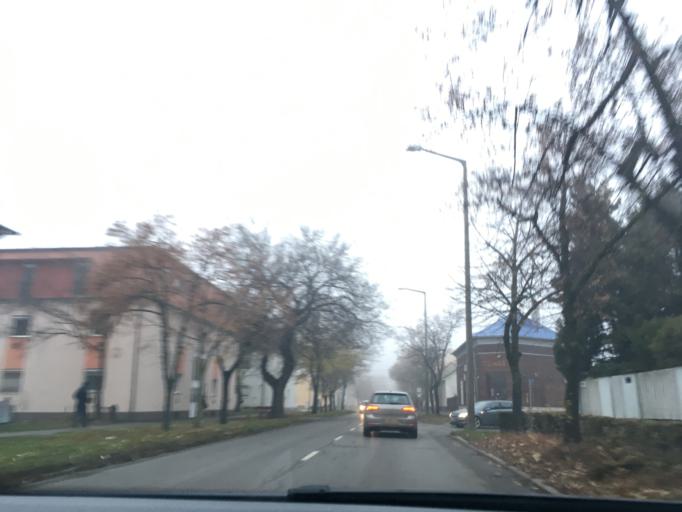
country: HU
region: Hajdu-Bihar
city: Debrecen
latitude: 47.5355
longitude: 21.6459
